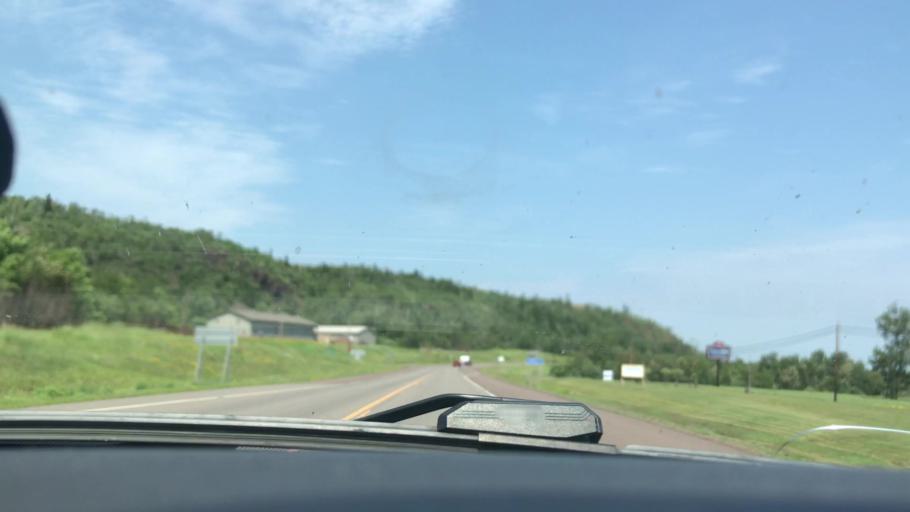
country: US
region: Minnesota
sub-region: Lake County
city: Silver Bay
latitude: 47.3003
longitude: -91.2527
